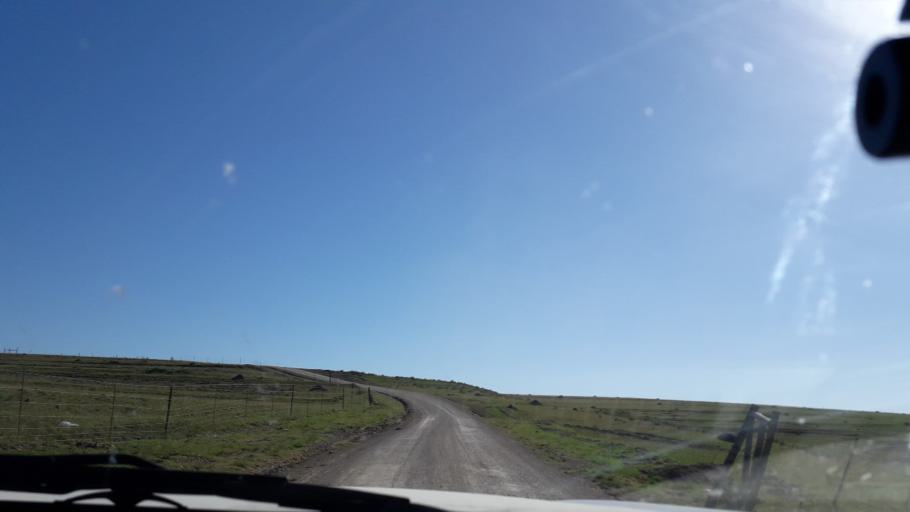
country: ZA
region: Eastern Cape
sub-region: Buffalo City Metropolitan Municipality
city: East London
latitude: -32.7982
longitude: 27.9556
